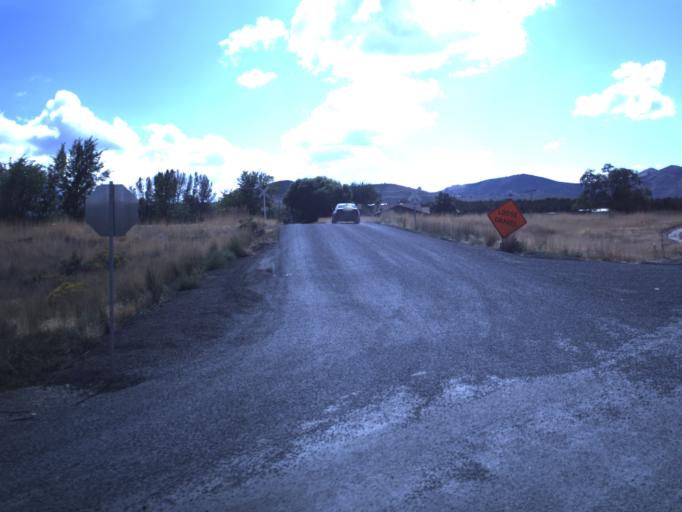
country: US
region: Utah
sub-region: Utah County
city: Genola
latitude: 39.9968
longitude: -111.8245
